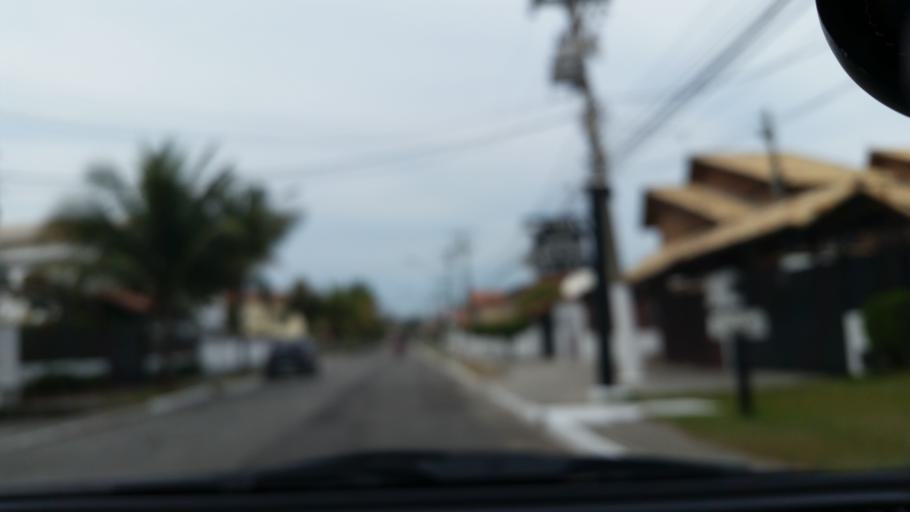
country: BR
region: Rio de Janeiro
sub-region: Cabo Frio
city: Cabo Frio
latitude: -22.8649
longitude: -41.9921
